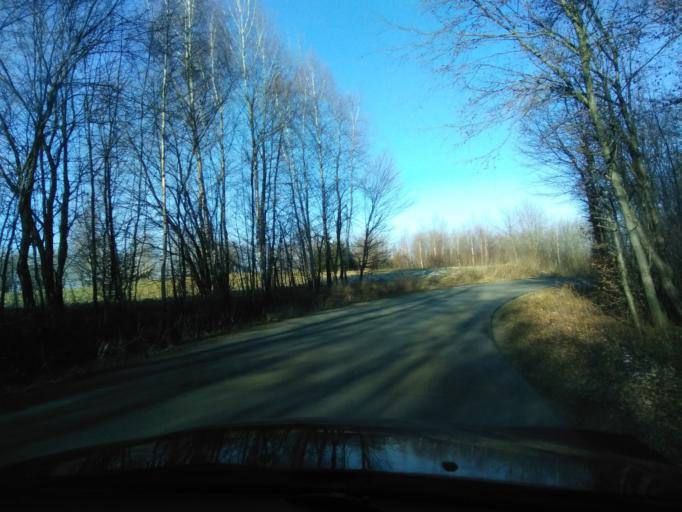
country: PL
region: Subcarpathian Voivodeship
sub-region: Powiat krosnienski
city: Rymanow
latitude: 49.5941
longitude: 21.8931
